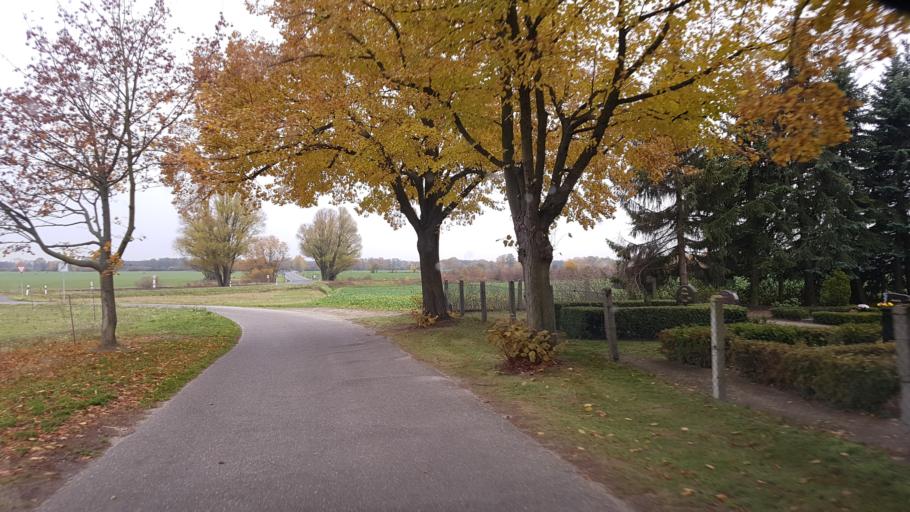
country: DE
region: Brandenburg
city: Finsterwalde
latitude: 51.6842
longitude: 13.7220
